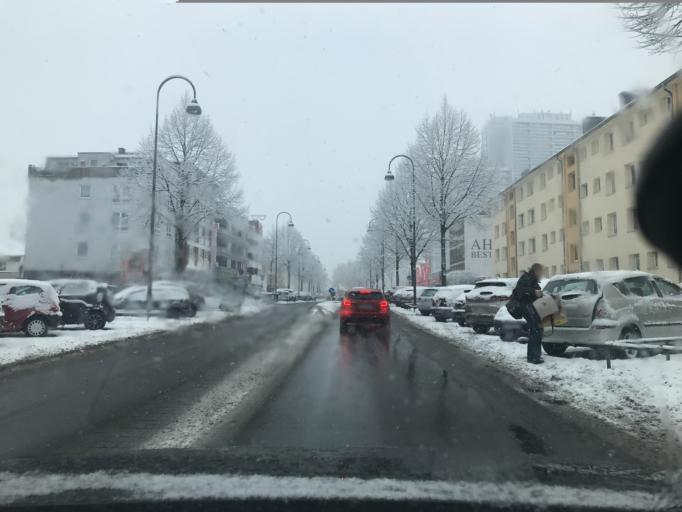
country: DE
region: North Rhine-Westphalia
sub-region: Regierungsbezirk Koln
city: Bilderstoeckchen
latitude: 50.9589
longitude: 6.8975
